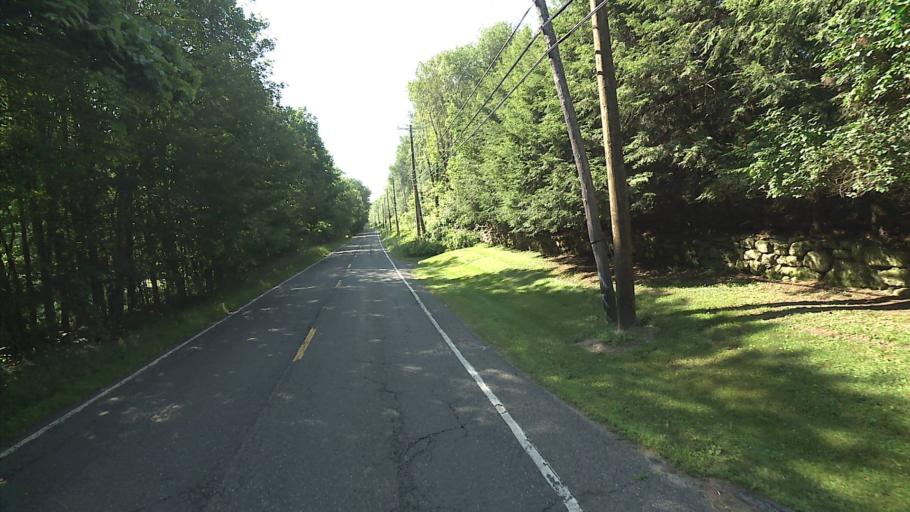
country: US
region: Connecticut
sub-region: Litchfield County
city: Winsted
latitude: 42.0021
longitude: -73.1041
